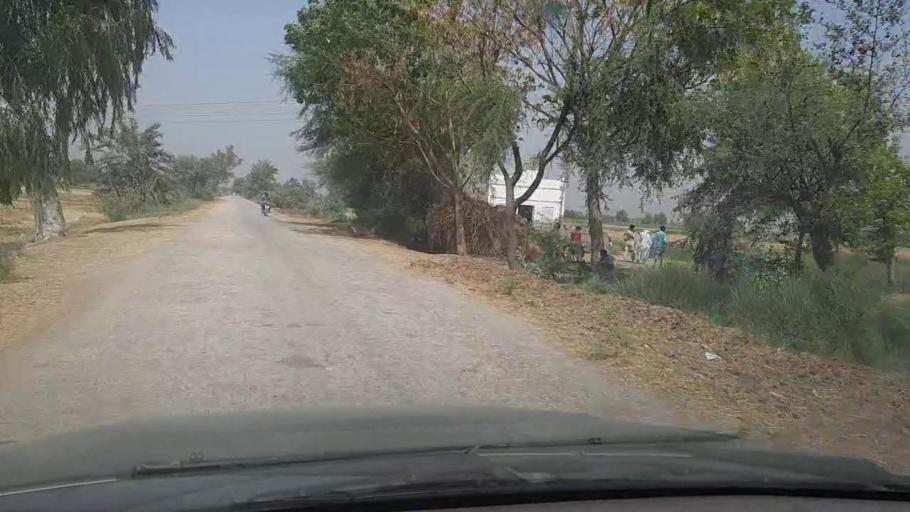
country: PK
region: Sindh
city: Madeji
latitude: 27.7936
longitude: 68.4909
